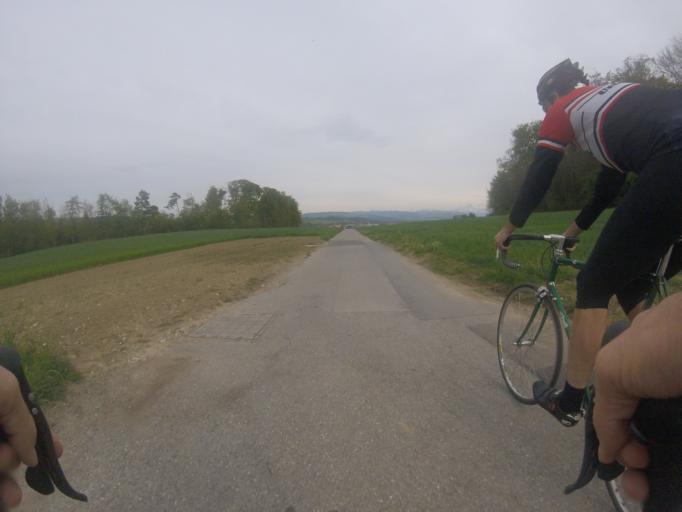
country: CH
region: Bern
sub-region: Bern-Mittelland District
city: Muri
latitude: 46.9181
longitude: 7.4860
